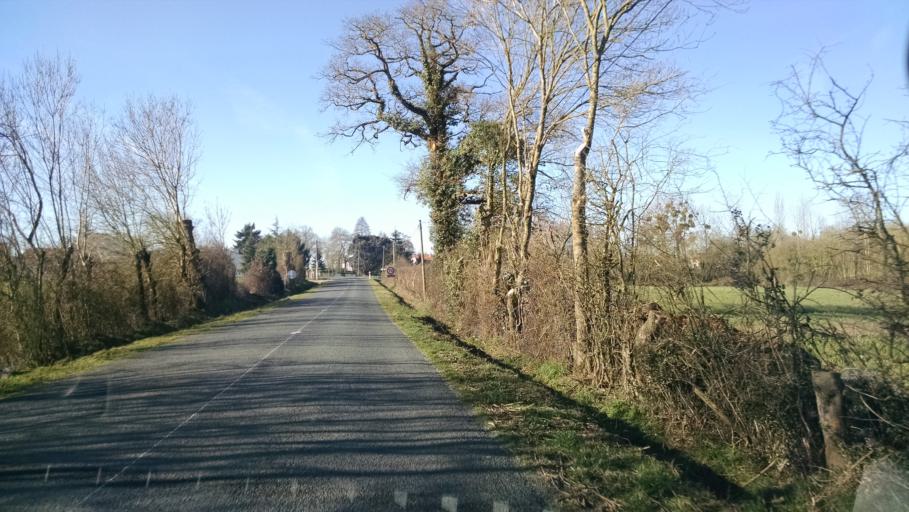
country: FR
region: Pays de la Loire
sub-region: Departement de la Vendee
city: Saint-Andre-Treize-Voies
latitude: 46.9247
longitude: -1.4250
